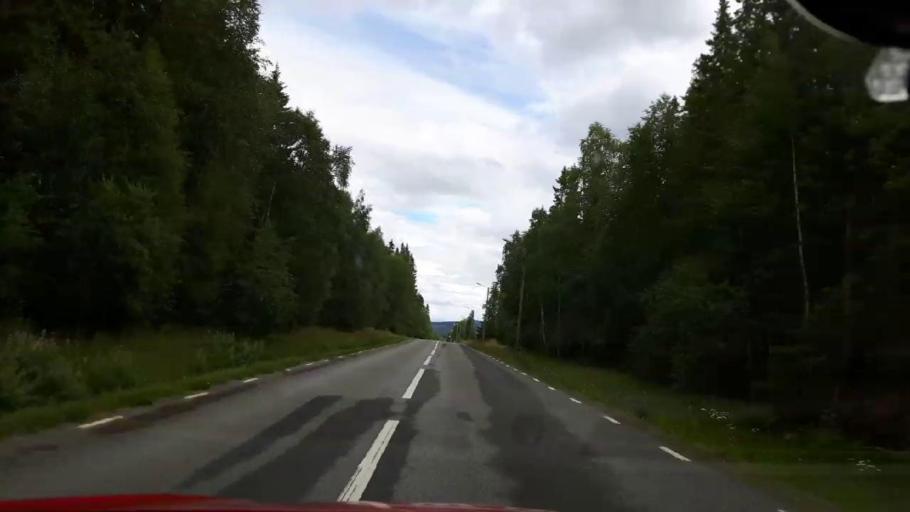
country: NO
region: Nord-Trondelag
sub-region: Lierne
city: Sandvika
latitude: 64.3903
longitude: 14.3823
